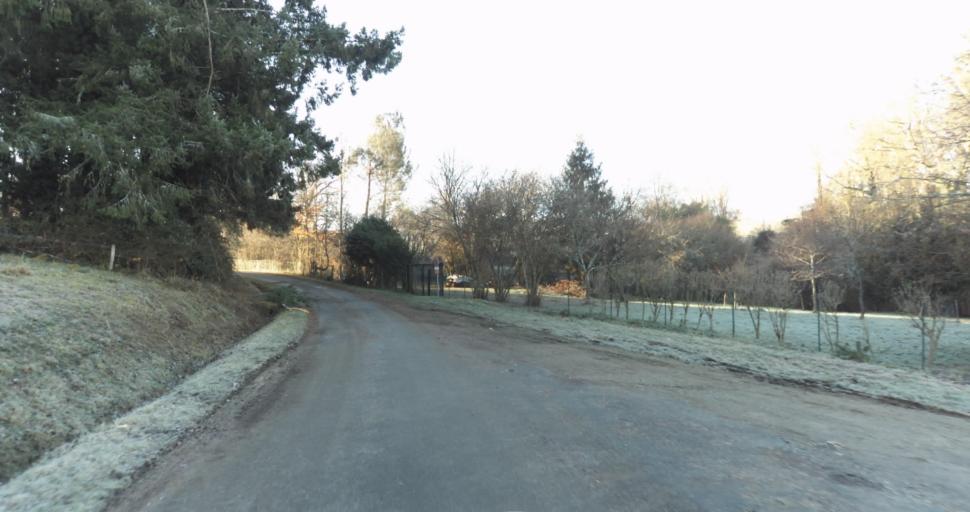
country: FR
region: Limousin
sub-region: Departement de la Haute-Vienne
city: Aixe-sur-Vienne
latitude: 45.8224
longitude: 1.1440
